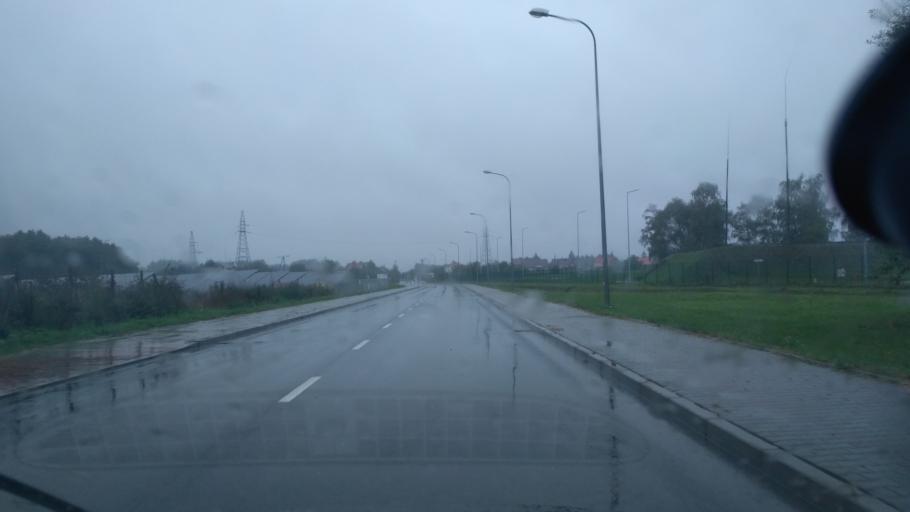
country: PL
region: Subcarpathian Voivodeship
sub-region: Powiat debicki
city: Debica
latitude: 50.0642
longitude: 21.4238
